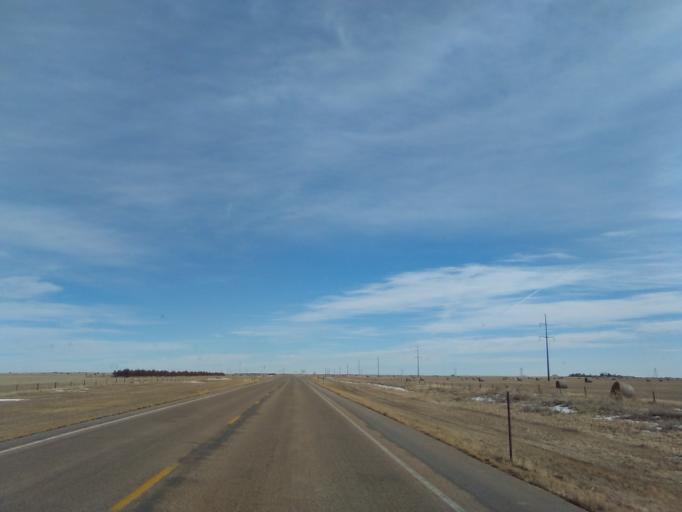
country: US
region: Wyoming
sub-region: Laramie County
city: Pine Bluffs
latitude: 41.4280
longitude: -104.3829
